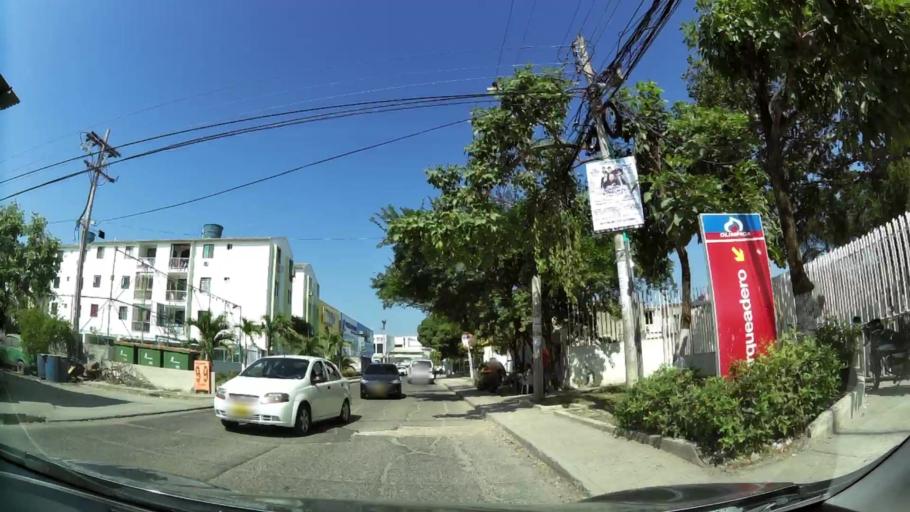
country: CO
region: Bolivar
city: Cartagena
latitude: 10.3822
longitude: -75.4692
